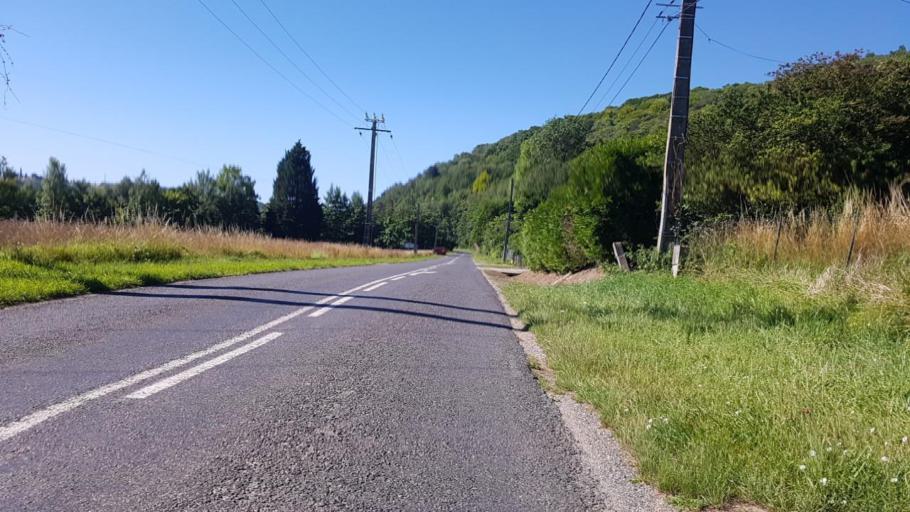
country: FR
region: Picardie
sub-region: Departement de l'Aisne
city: Chezy-sur-Marne
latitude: 48.9998
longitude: 3.3424
